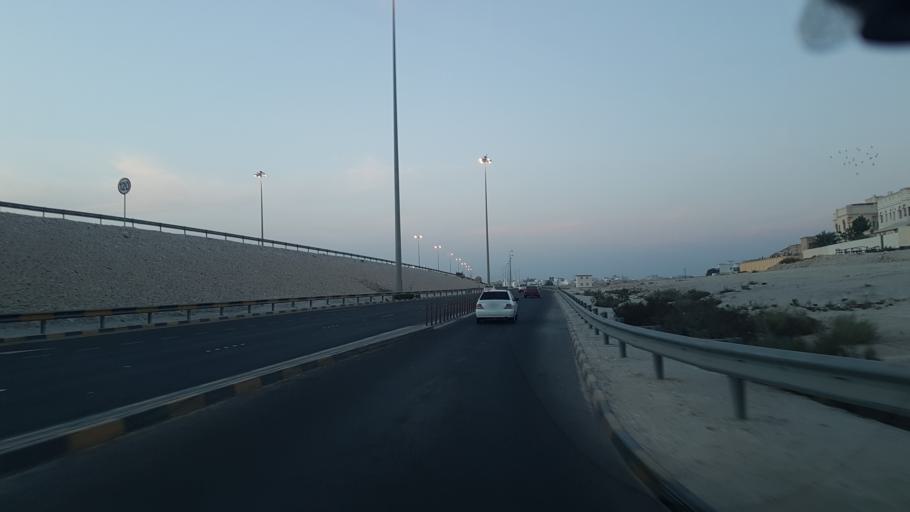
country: BH
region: Central Governorate
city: Madinat Hamad
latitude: 26.1405
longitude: 50.5111
